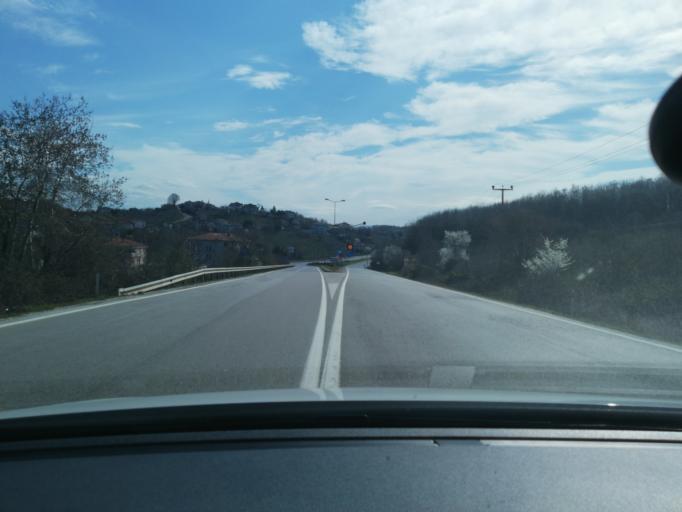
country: TR
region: Duzce
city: Akcakoca
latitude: 41.0872
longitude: 31.1508
